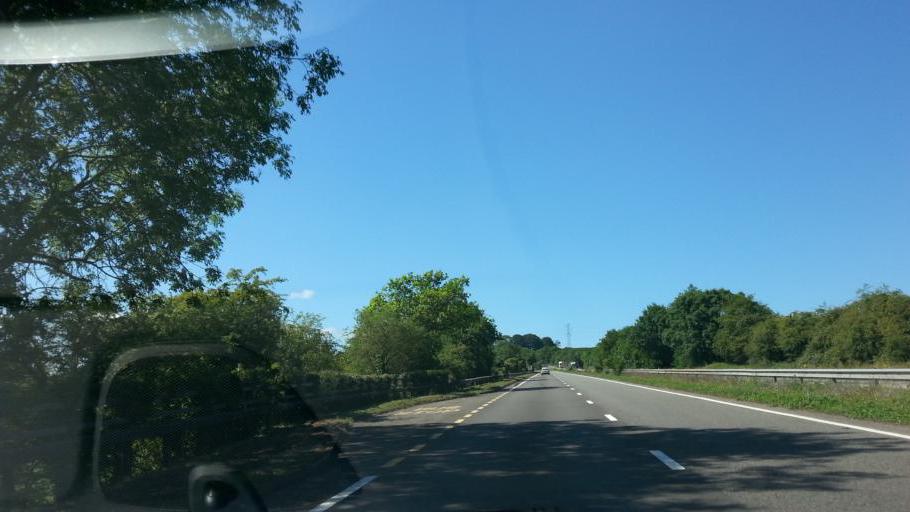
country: GB
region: England
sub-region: Herefordshire
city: Marstow
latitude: 51.8959
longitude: -2.6325
